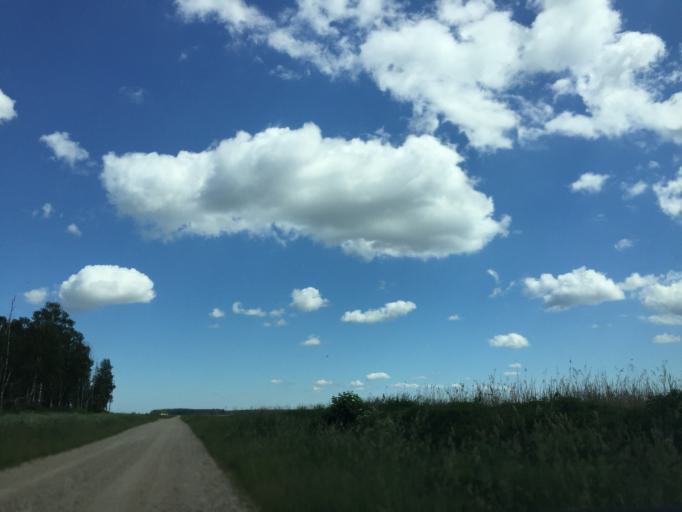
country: LV
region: Olaine
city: Olaine
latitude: 56.8557
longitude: 23.9457
